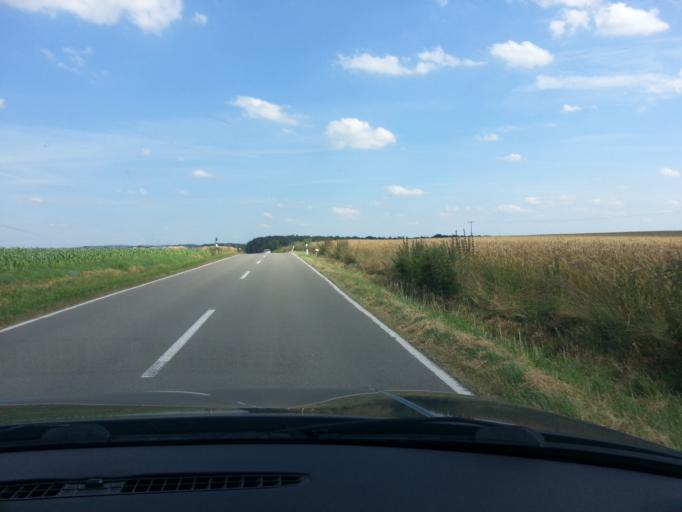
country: DE
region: Rheinland-Pfalz
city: Kleinsteinhausen
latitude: 49.1921
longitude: 7.4736
